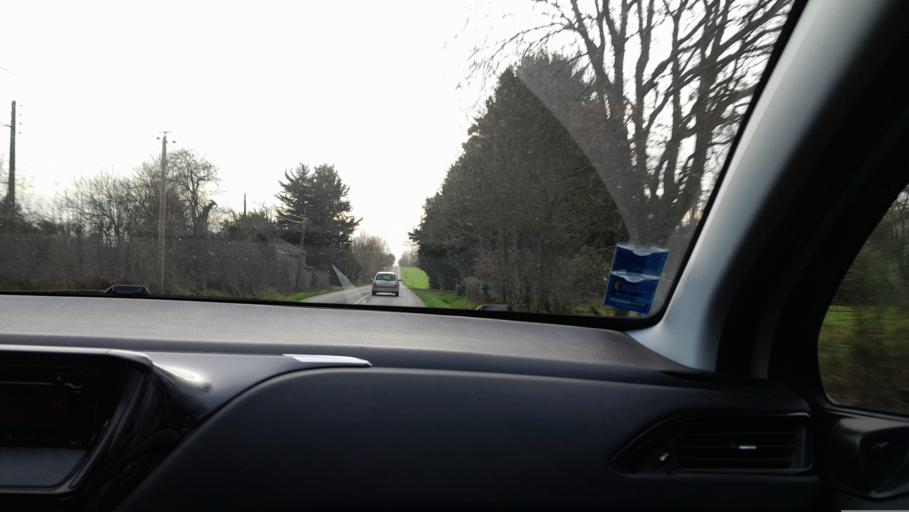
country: FR
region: Pays de la Loire
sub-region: Departement de la Mayenne
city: Ballots
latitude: 47.8890
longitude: -1.0360
